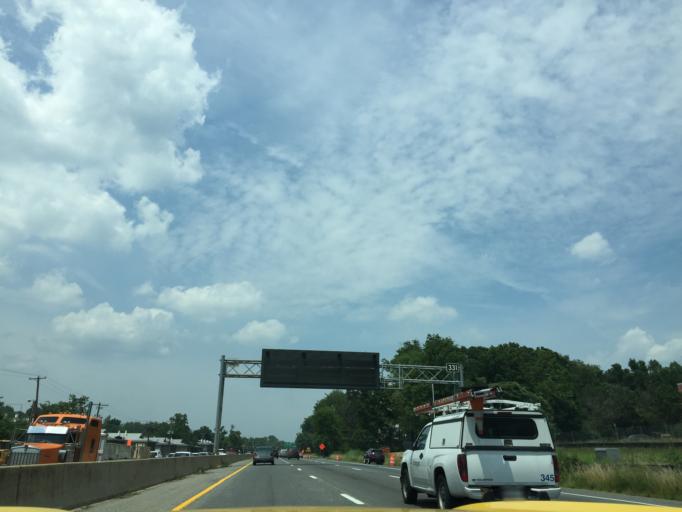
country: US
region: Maryland
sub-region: Prince George's County
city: Oxon Hill
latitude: 38.7831
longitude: -76.9978
